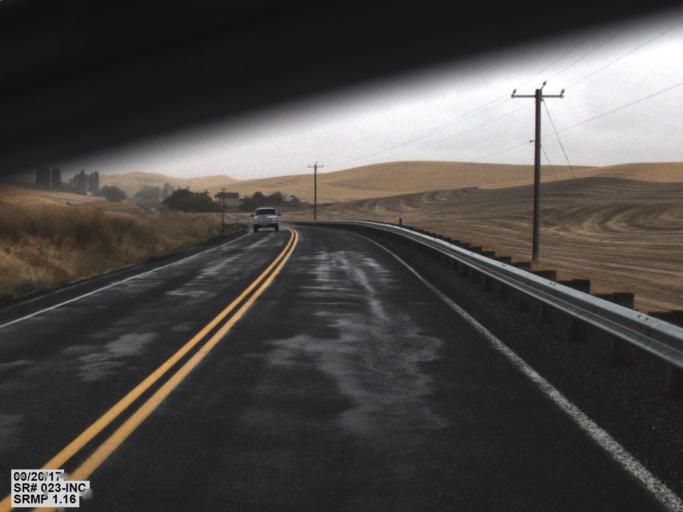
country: US
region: Washington
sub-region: Whitman County
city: Colfax
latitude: 47.0048
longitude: -117.3775
